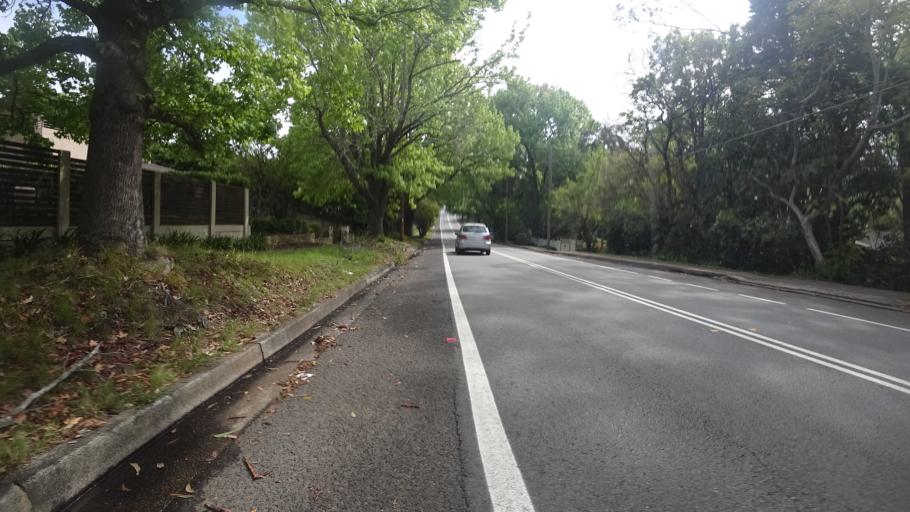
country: AU
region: New South Wales
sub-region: City of Sydney
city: Pymble
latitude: -33.7319
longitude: 151.1381
